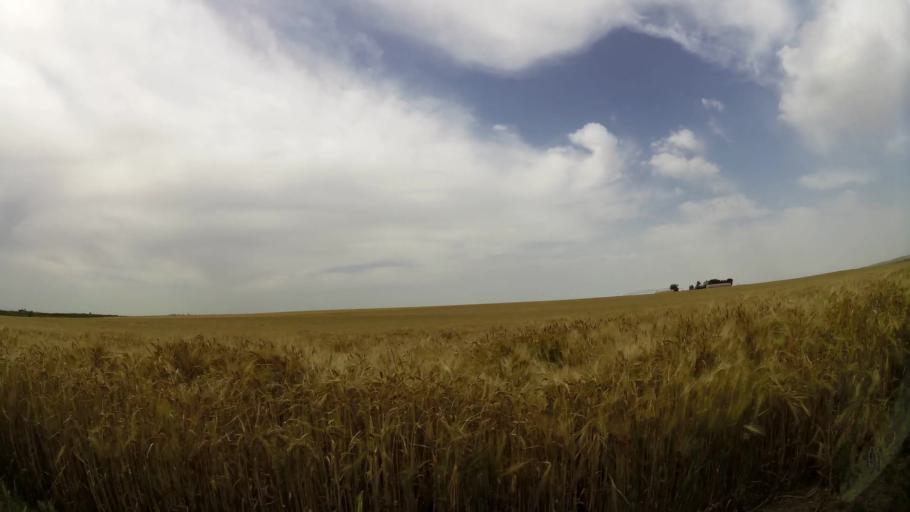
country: MA
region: Rabat-Sale-Zemmour-Zaer
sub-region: Khemisset
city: Tiflet
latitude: 33.7580
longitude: -6.2192
